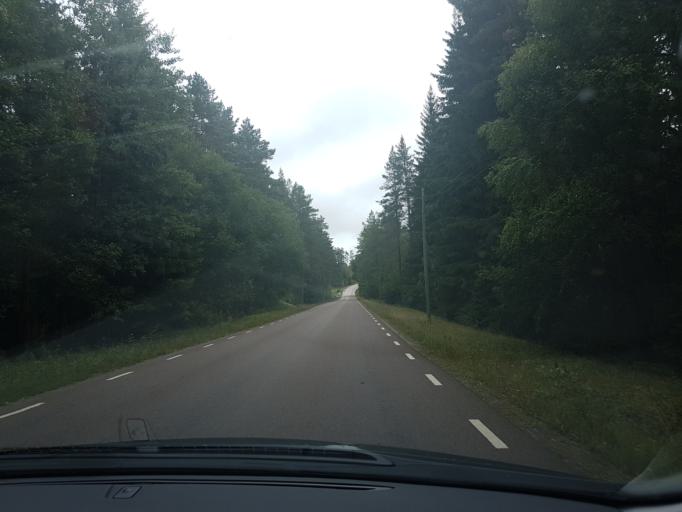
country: SE
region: Joenkoeping
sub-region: Vetlanda Kommun
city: Vetlanda
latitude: 57.3198
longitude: 15.1415
